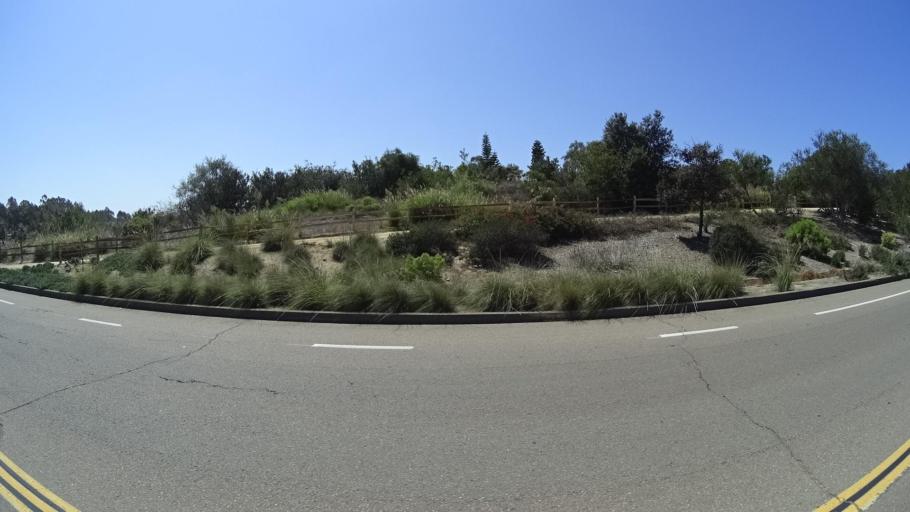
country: US
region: California
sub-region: San Diego County
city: Fairbanks Ranch
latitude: 32.9984
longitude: -117.1579
